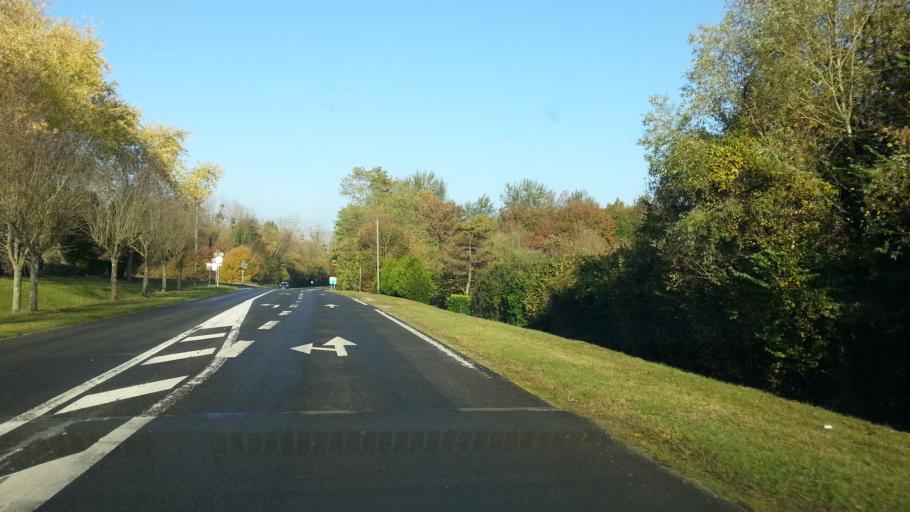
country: FR
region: Picardie
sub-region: Departement de l'Oise
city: Balagny-sur-Therain
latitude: 49.3036
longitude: 2.3308
